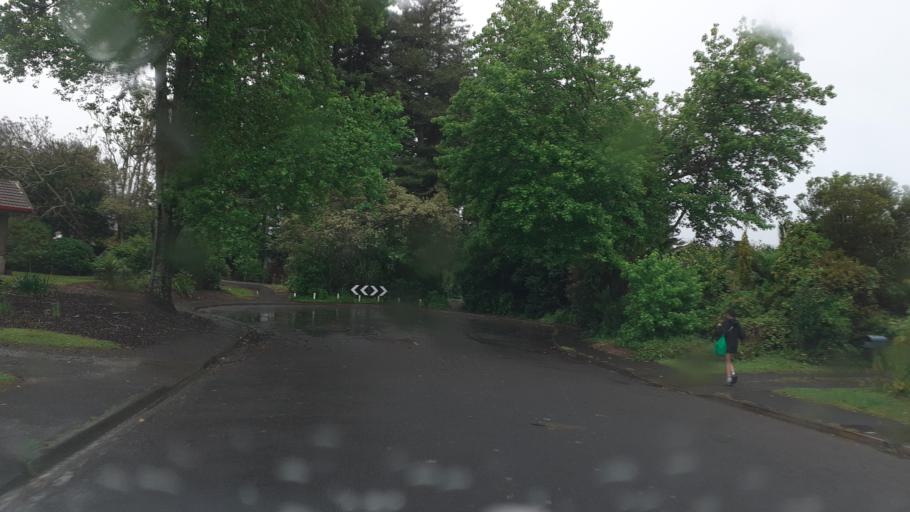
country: NZ
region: Northland
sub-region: Far North District
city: Kerikeri
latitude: -35.2233
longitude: 173.9555
